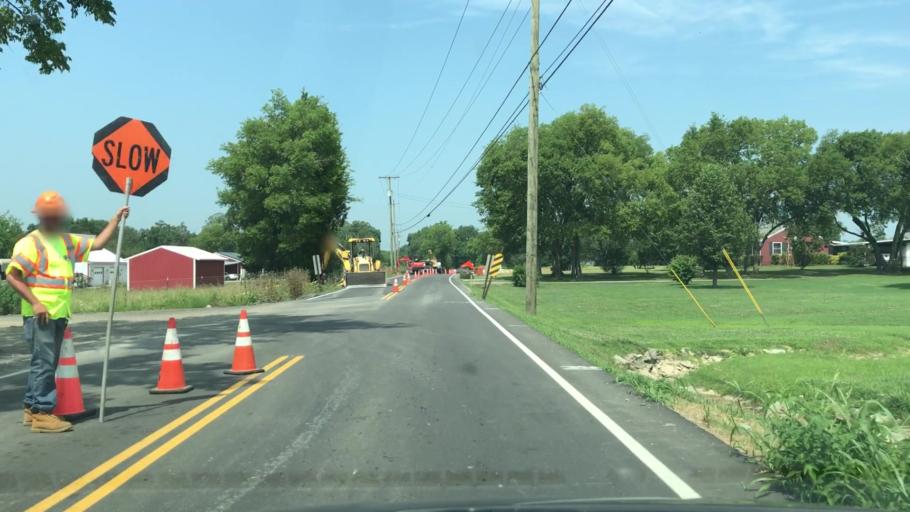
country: US
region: Tennessee
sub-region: Wilson County
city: Rural Hill
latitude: 36.1133
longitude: -86.4308
